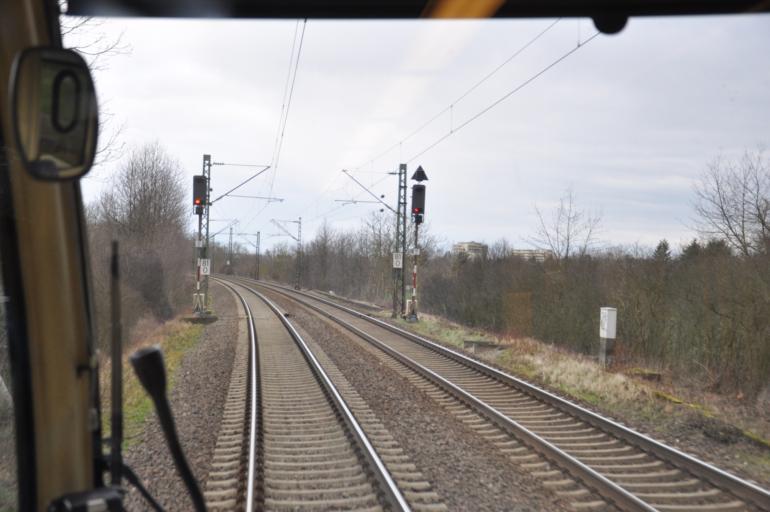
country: DE
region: Baden-Wuerttemberg
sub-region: Karlsruhe Region
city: Ettlingen
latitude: 48.9342
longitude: 8.3847
